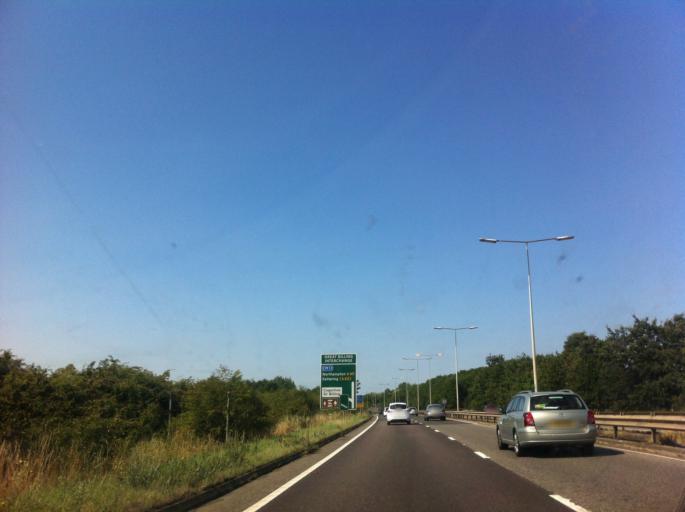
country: GB
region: England
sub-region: Northamptonshire
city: Earls Barton
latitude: 52.2541
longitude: -0.7981
